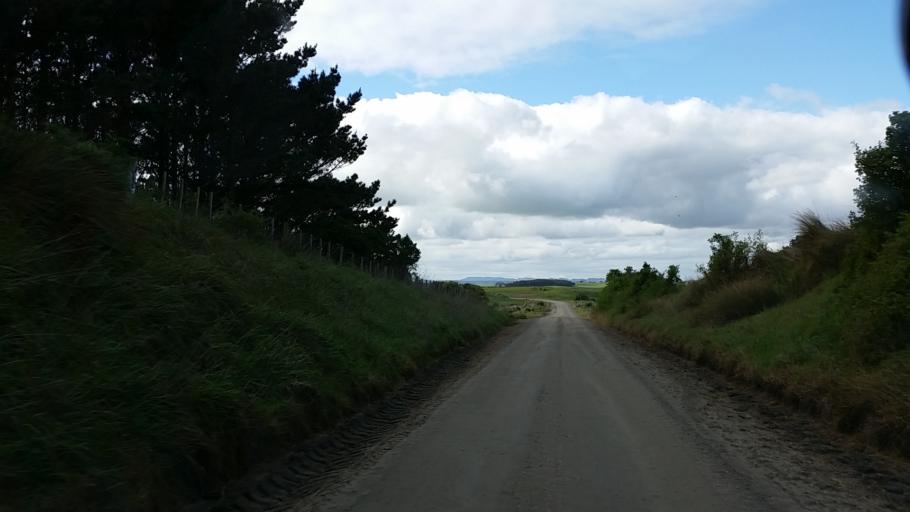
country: NZ
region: Taranaki
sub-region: South Taranaki District
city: Patea
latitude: -39.8003
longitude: 174.6042
